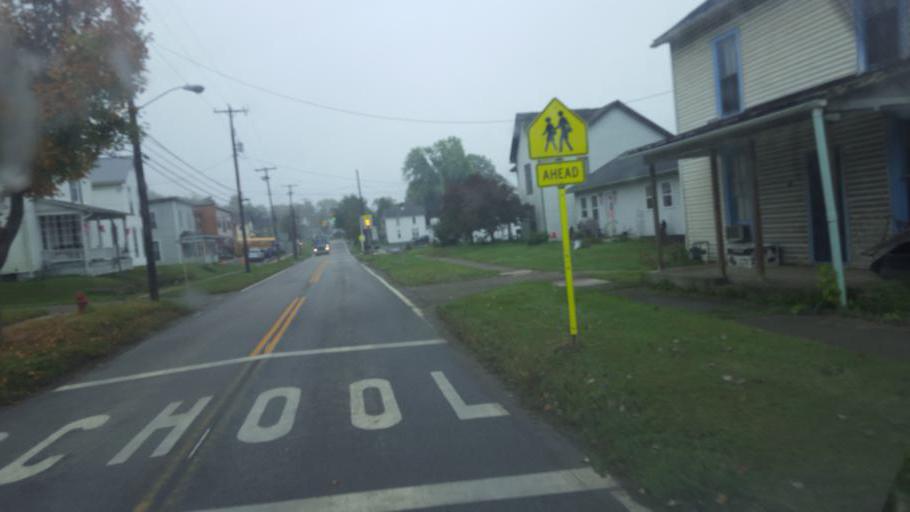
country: US
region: Ohio
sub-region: Harrison County
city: Cadiz
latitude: 40.4001
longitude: -81.0889
